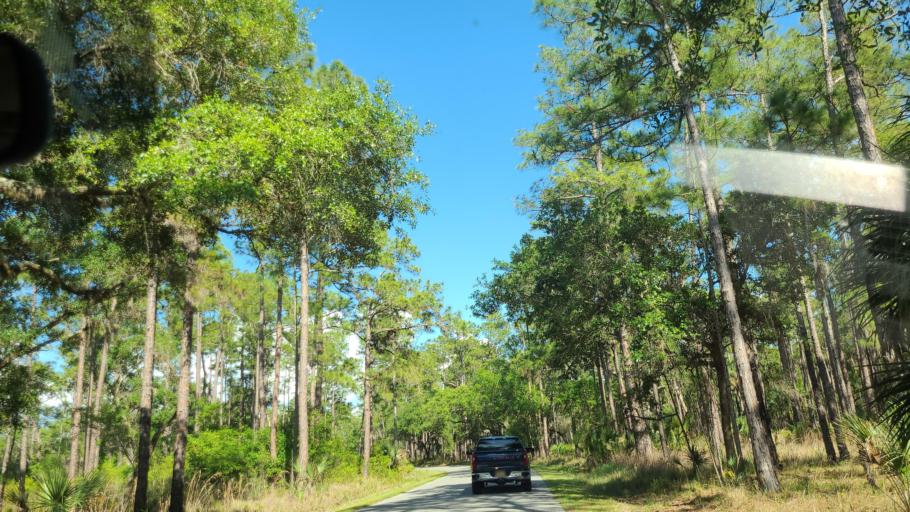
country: US
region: Florida
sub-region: Polk County
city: Babson Park
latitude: 27.9523
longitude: -81.3719
